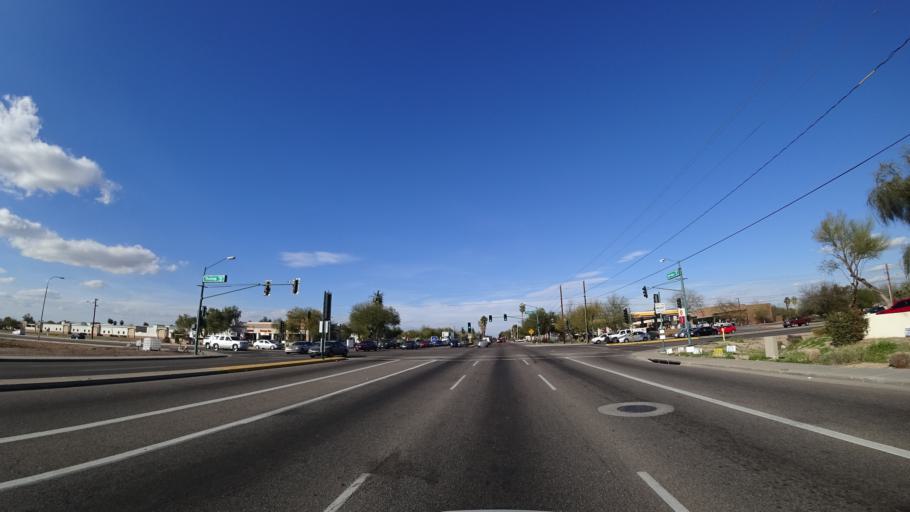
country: US
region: Arizona
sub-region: Maricopa County
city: Tolleson
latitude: 33.4792
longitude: -112.2377
